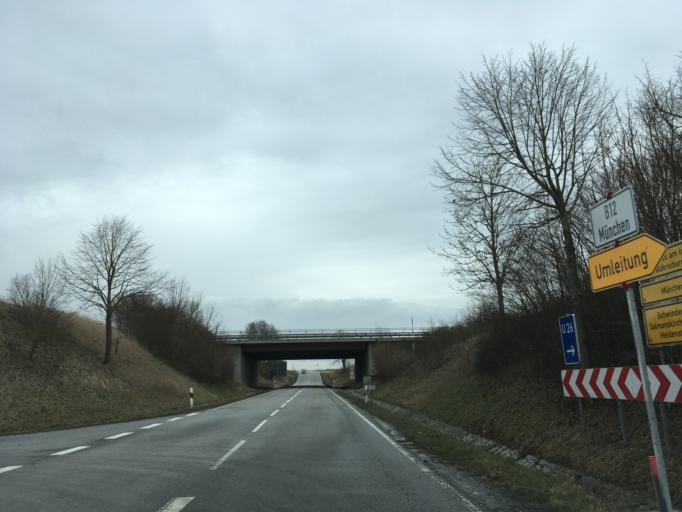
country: DE
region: Bavaria
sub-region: Upper Bavaria
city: Ampfing
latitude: 48.2516
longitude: 12.3887
